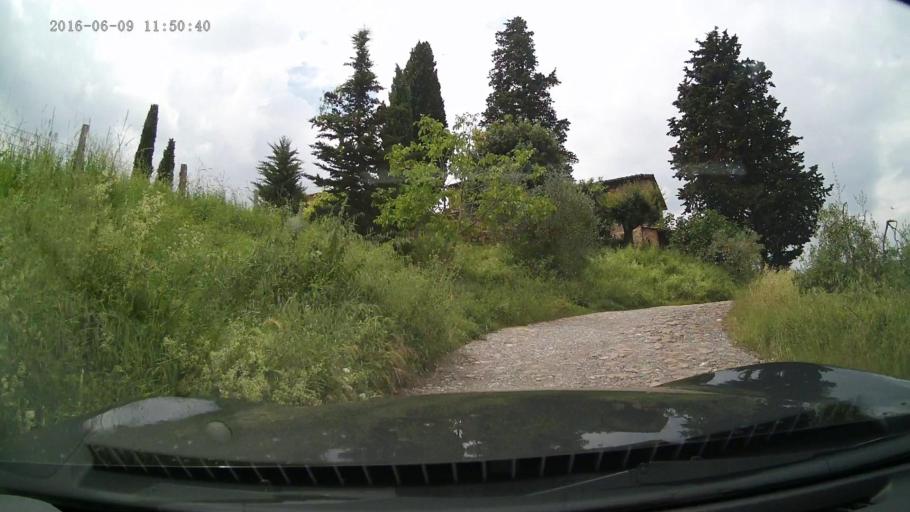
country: IT
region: Tuscany
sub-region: Province of Florence
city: Greve in Chianti
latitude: 43.5663
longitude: 11.2966
